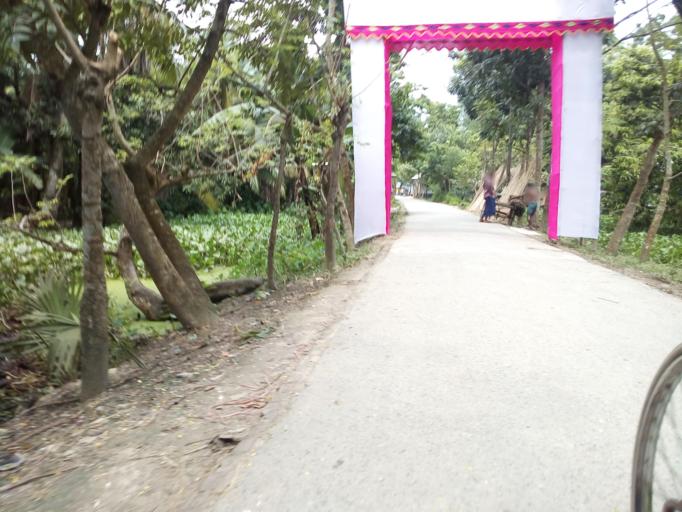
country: BD
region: Khulna
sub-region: Magura
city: Magura
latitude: 23.5307
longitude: 89.5467
